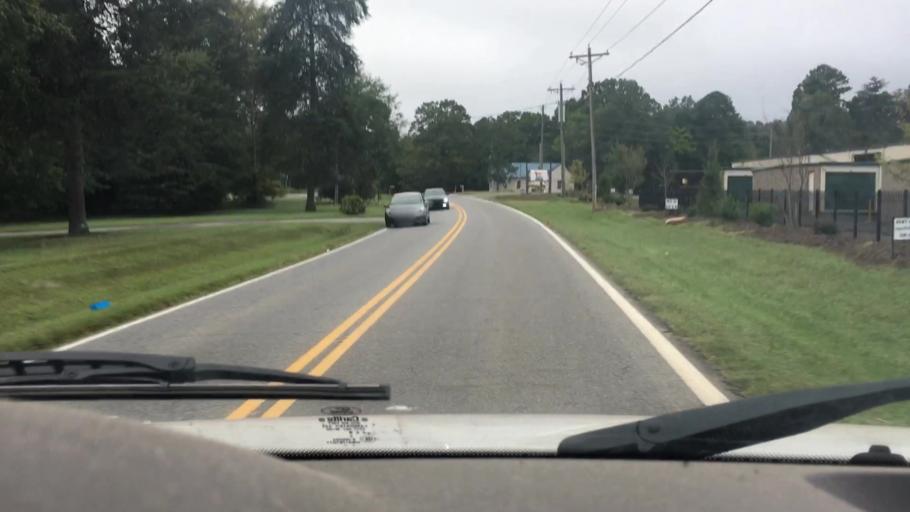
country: US
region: North Carolina
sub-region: Lincoln County
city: Denver
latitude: 35.5398
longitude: -81.0199
